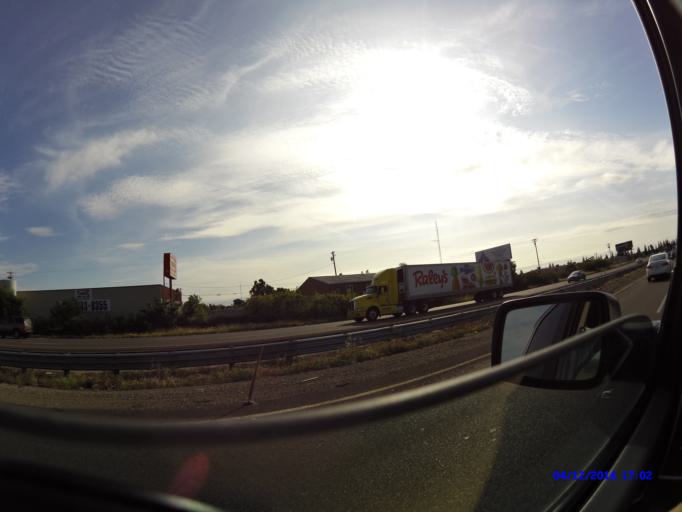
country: US
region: California
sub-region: Stanislaus County
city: Salida
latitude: 37.7125
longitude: -121.0870
